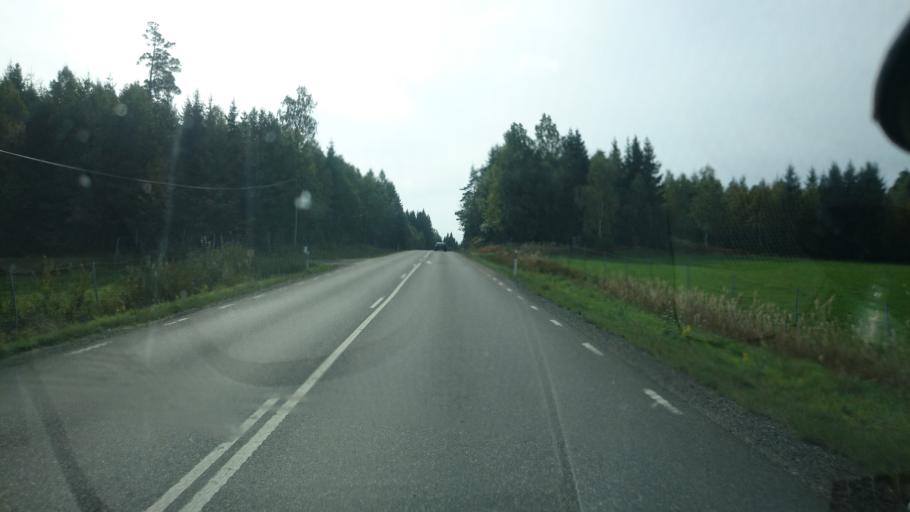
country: SE
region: Vaestra Goetaland
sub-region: Alingsas Kommun
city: Alingsas
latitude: 58.0034
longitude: 12.4438
